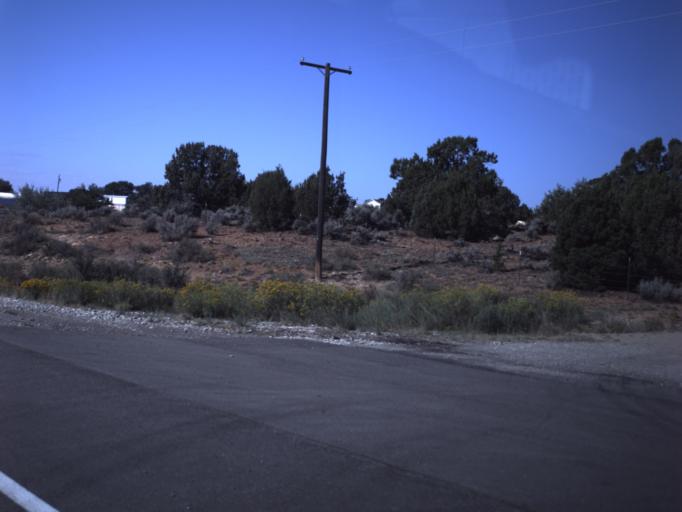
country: US
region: Utah
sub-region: San Juan County
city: Blanding
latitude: 37.6516
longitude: -109.4598
